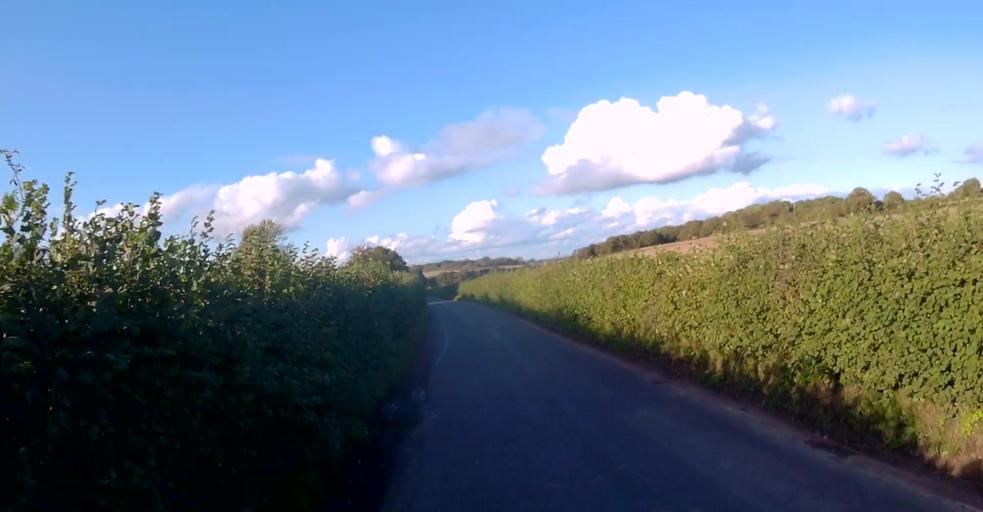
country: GB
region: England
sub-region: Hampshire
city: Long Sutton
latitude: 51.2275
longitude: -0.9239
